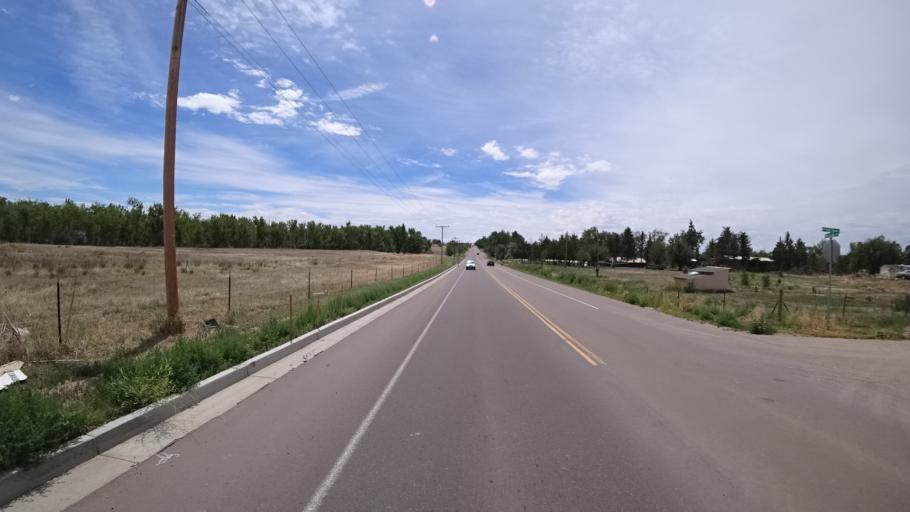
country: US
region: Colorado
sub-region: El Paso County
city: Fountain
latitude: 38.7038
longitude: -104.6736
